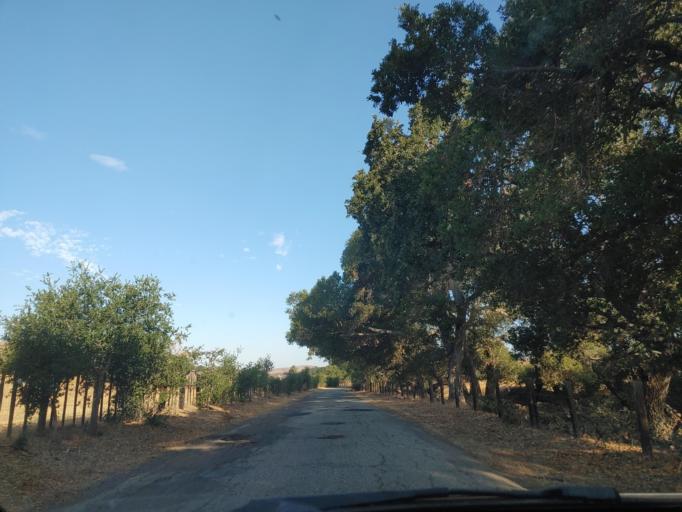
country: US
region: California
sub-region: San Benito County
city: Ridgemark
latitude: 36.7828
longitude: -121.2482
